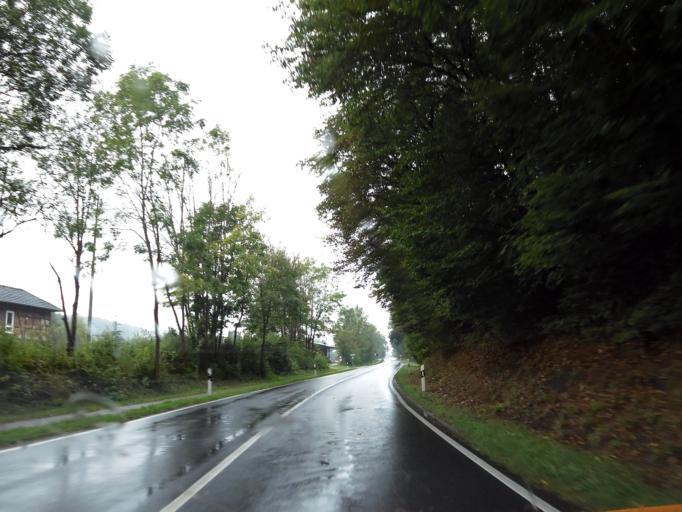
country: DE
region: Lower Saxony
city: Bad Lauterberg im Harz
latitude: 51.6237
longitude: 10.4049
